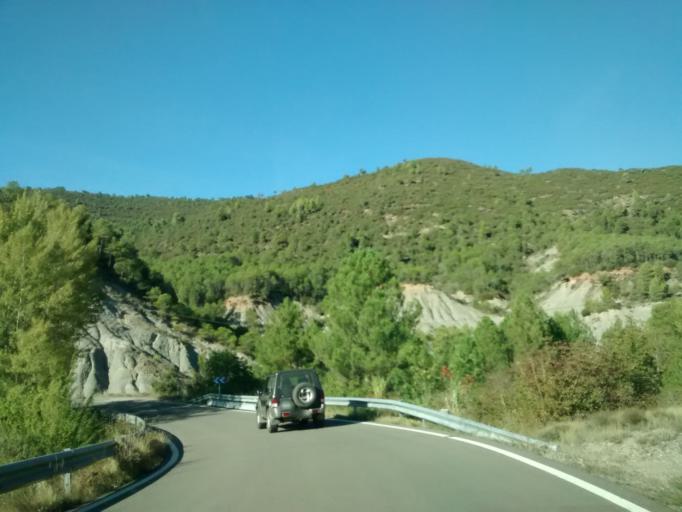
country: ES
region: Aragon
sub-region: Provincia de Huesca
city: Loarre
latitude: 42.3857
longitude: -0.6998
